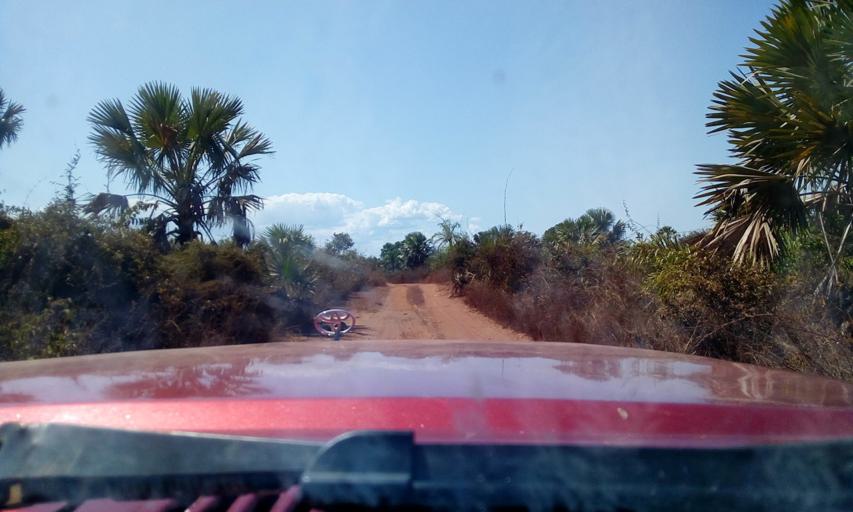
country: MG
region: Boeny
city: Sitampiky
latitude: -16.1272
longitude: 45.4288
